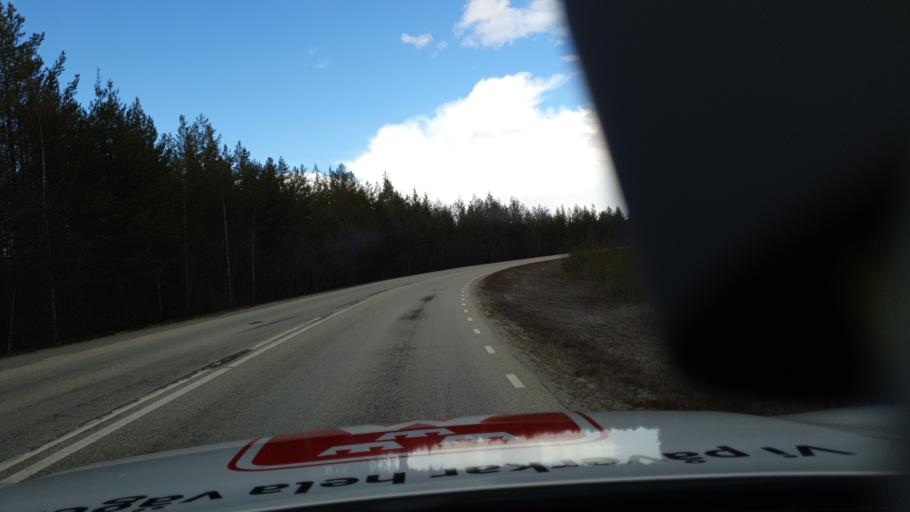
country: SE
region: Jaemtland
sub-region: Harjedalens Kommun
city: Sveg
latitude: 62.4159
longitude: 13.7694
